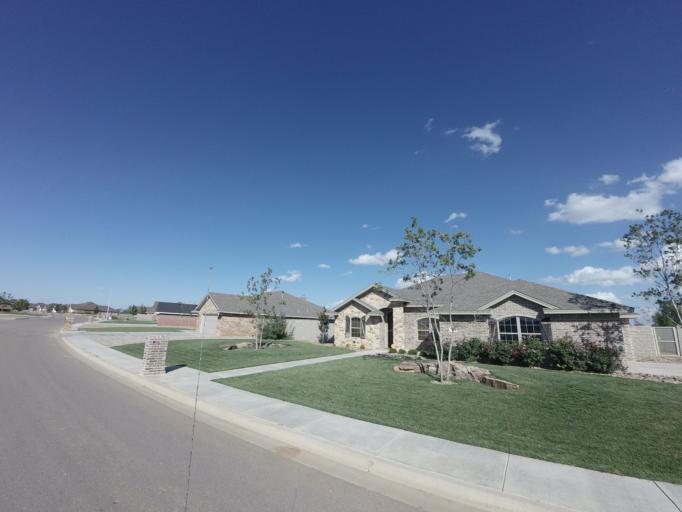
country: US
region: New Mexico
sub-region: Curry County
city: Clovis
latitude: 34.4364
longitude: -103.1737
